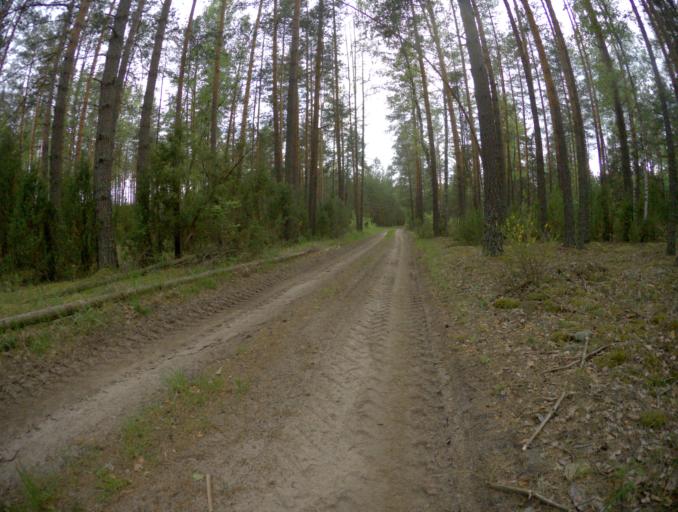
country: RU
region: Rjazan
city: Gus'-Zheleznyy
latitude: 55.1254
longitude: 41.1411
